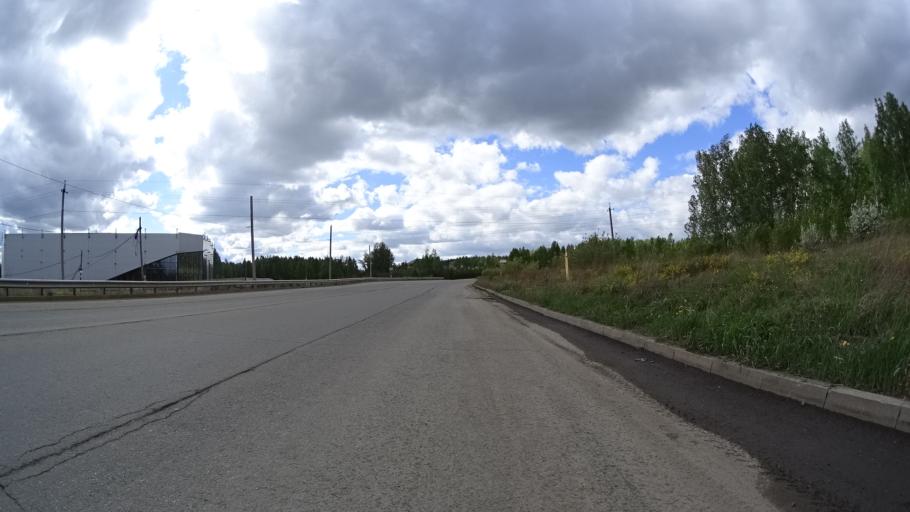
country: RU
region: Chelyabinsk
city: Sargazy
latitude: 55.1532
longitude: 61.2673
